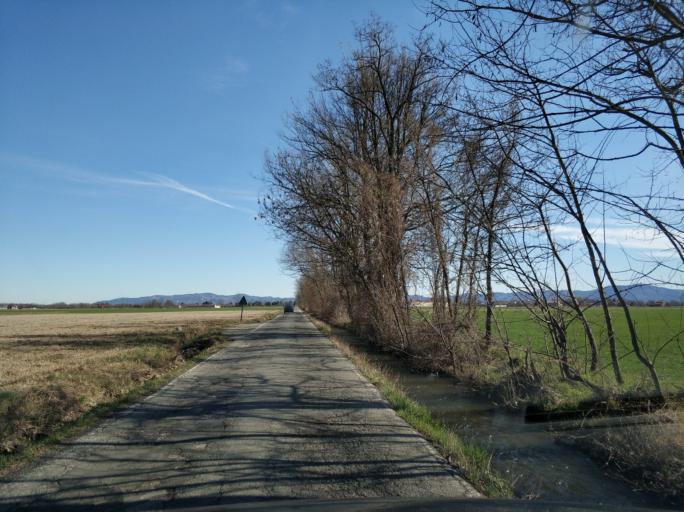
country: IT
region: Piedmont
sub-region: Provincia di Torino
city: San Francesco al Campo
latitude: 45.1973
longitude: 7.6783
